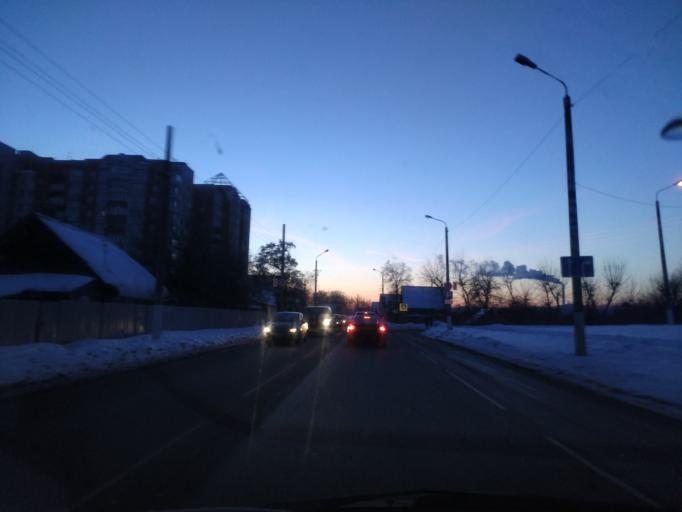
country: BY
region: Mogilev
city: Mahilyow
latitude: 53.8837
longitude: 30.3280
